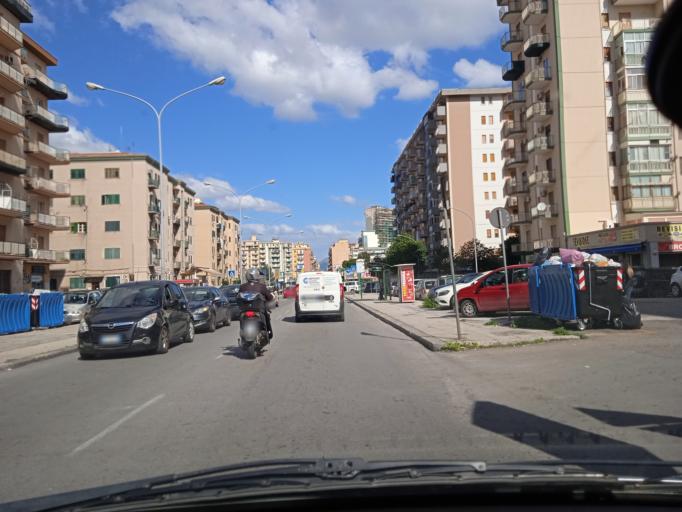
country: IT
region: Sicily
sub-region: Palermo
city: Ciaculli
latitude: 38.0998
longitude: 13.3718
